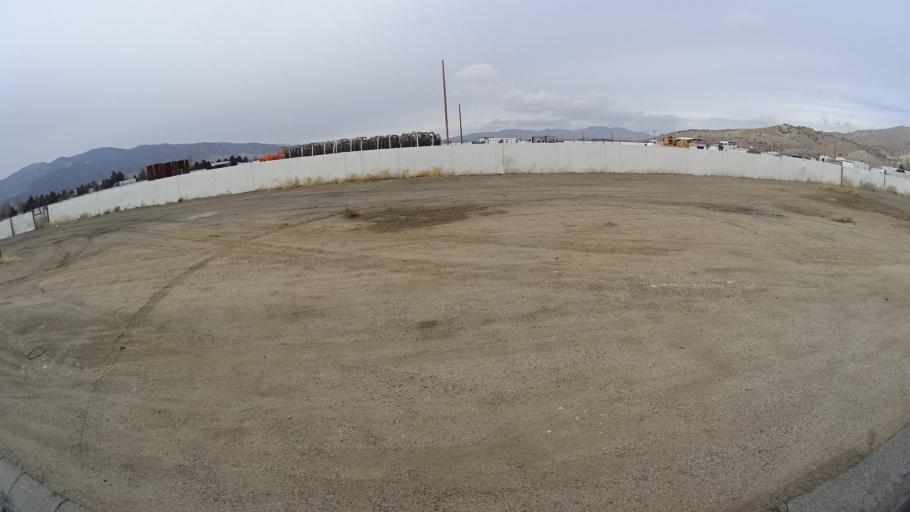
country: US
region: California
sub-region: Kern County
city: Tehachapi
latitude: 35.1232
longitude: -118.3963
